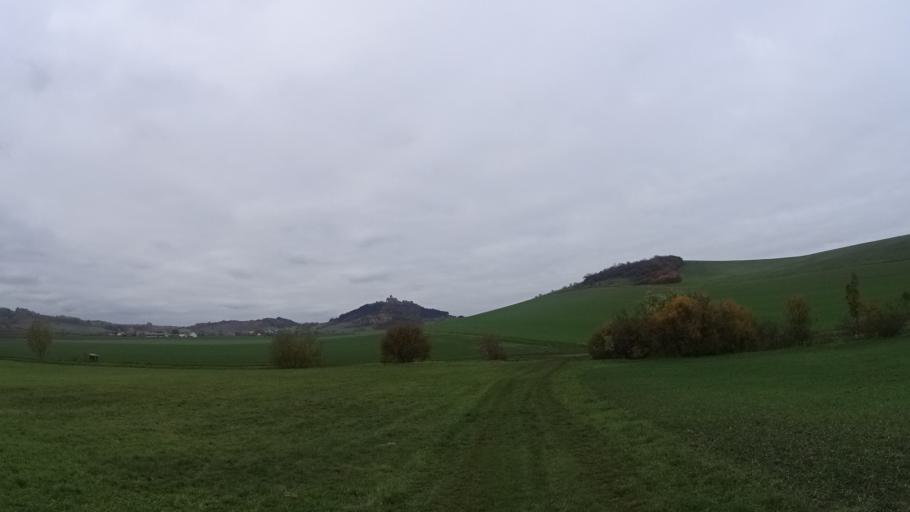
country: DE
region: Thuringia
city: Arnstadt
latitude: 50.8543
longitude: 10.9056
